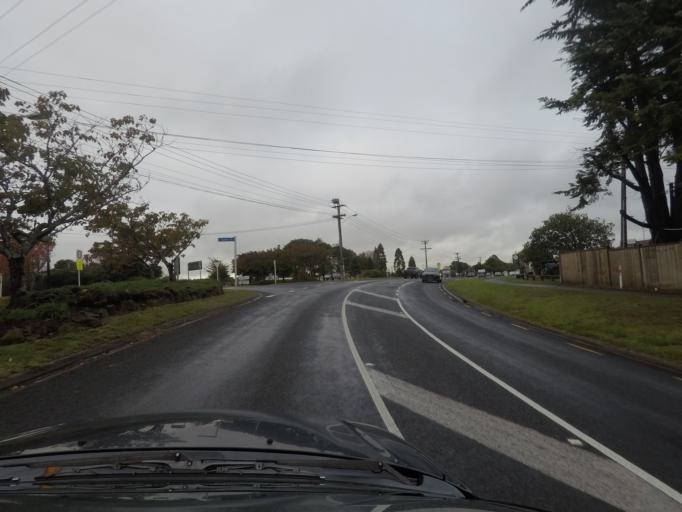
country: NZ
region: Auckland
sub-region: Auckland
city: Rosebank
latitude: -36.7577
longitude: 174.5920
